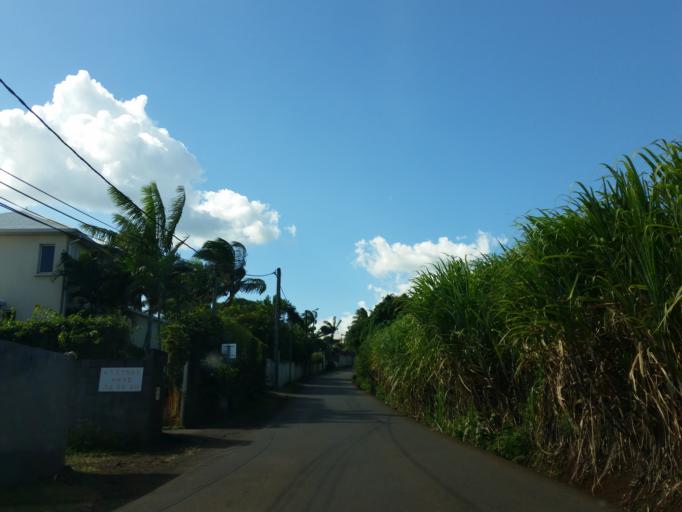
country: RE
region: Reunion
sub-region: Reunion
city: Saint-Pierre
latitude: -21.3278
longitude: 55.4964
